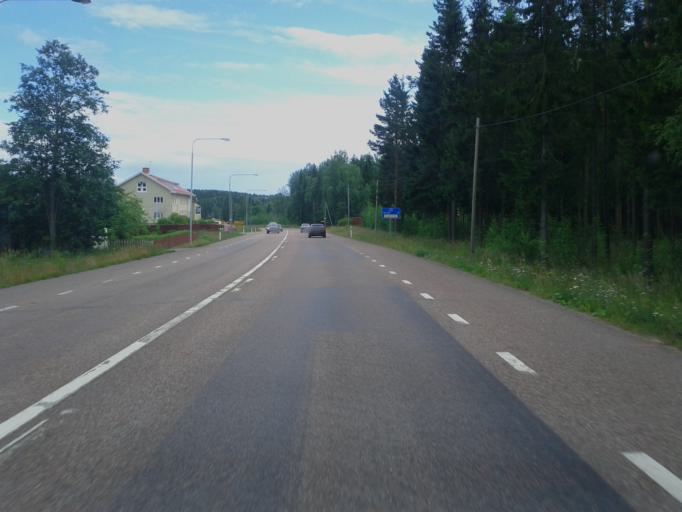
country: SE
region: Dalarna
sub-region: Faluns Kommun
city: Bjursas
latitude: 60.7229
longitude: 15.4492
